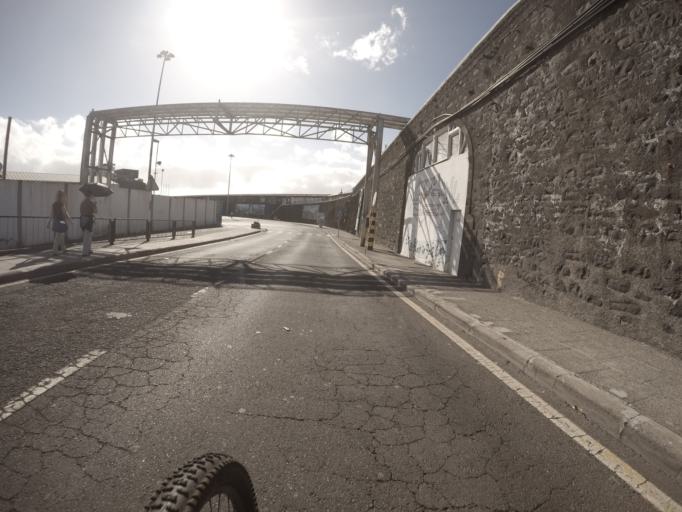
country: PT
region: Madeira
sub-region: Funchal
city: Funchal
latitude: 32.6416
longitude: -16.9179
